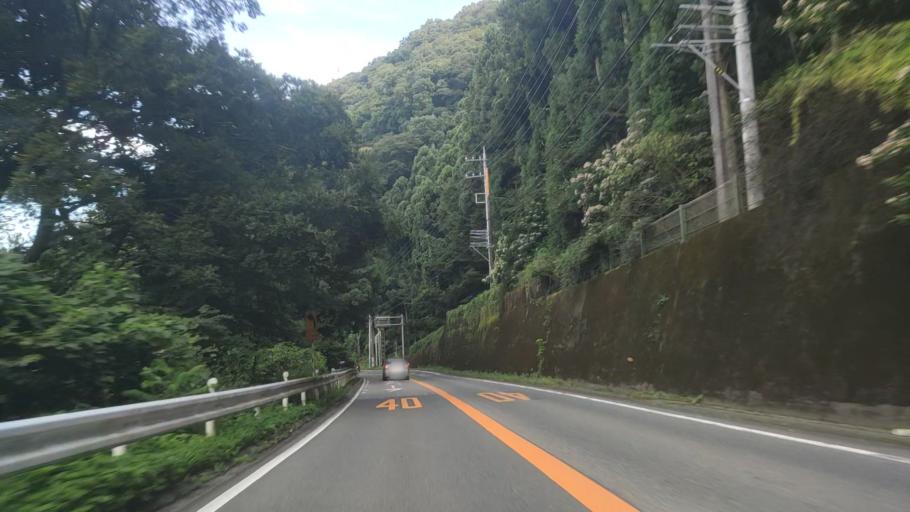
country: JP
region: Gunma
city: Omamacho-omama
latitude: 36.4518
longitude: 139.2697
